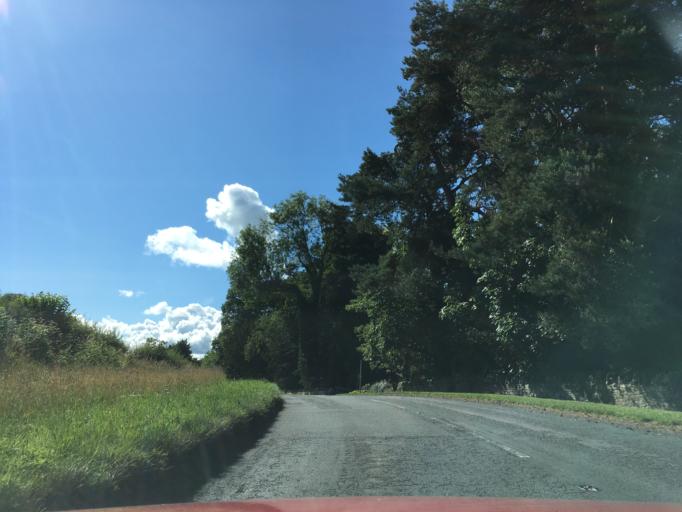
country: GB
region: England
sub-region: Herefordshire
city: Yatton
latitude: 51.9652
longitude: -2.5504
